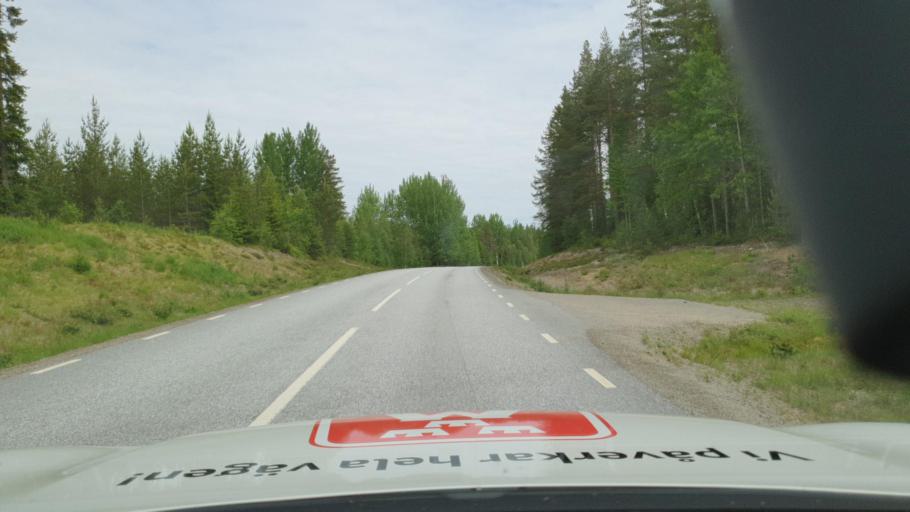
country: SE
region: Vaesterbotten
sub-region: Umea Kommun
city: Ersmark
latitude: 64.2853
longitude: 20.2222
